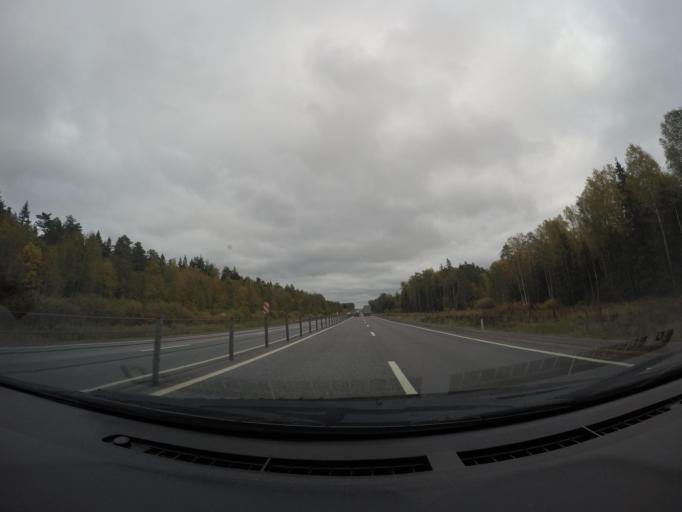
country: RU
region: Moskovskaya
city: Tuchkovo
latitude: 55.5458
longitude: 36.4381
